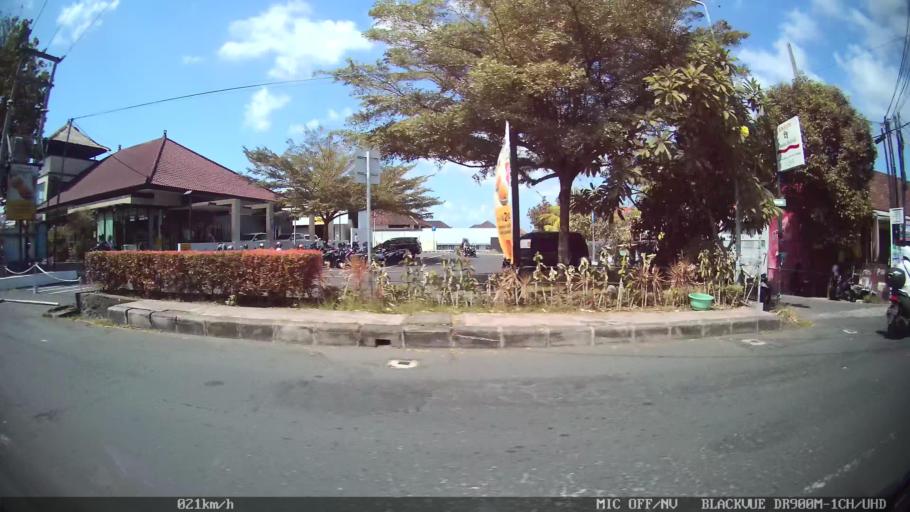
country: ID
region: Bali
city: Banjar Kertasari
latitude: -8.6376
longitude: 115.1860
